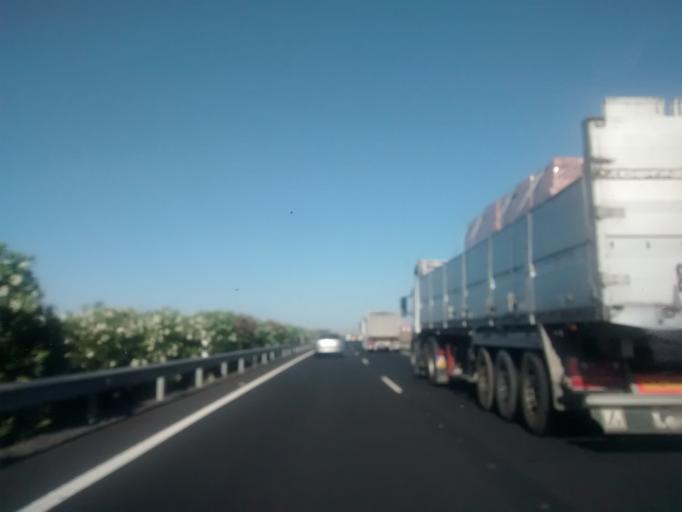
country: ES
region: Andalusia
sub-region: Provincia de Huelva
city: San Juan del Puerto
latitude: 37.3336
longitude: -6.7899
